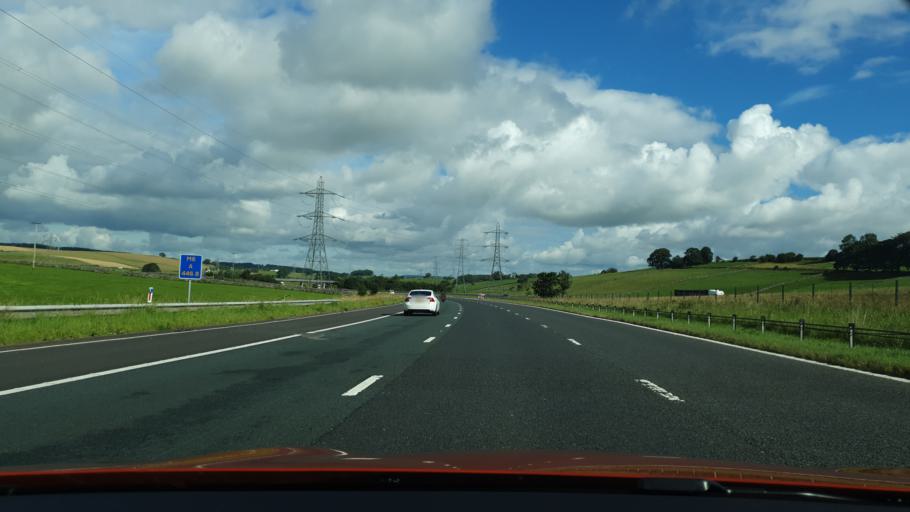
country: GB
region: England
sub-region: Cumbria
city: Penrith
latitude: 54.5552
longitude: -2.6734
